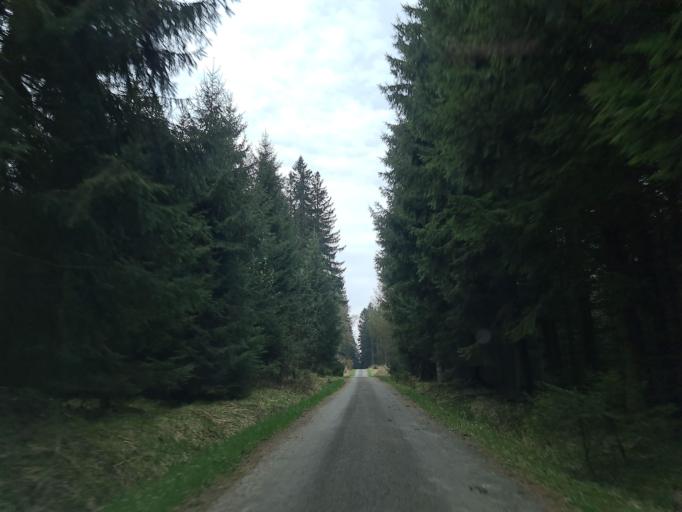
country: DE
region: Saxony
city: Ellefeld
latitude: 50.4587
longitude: 12.3894
